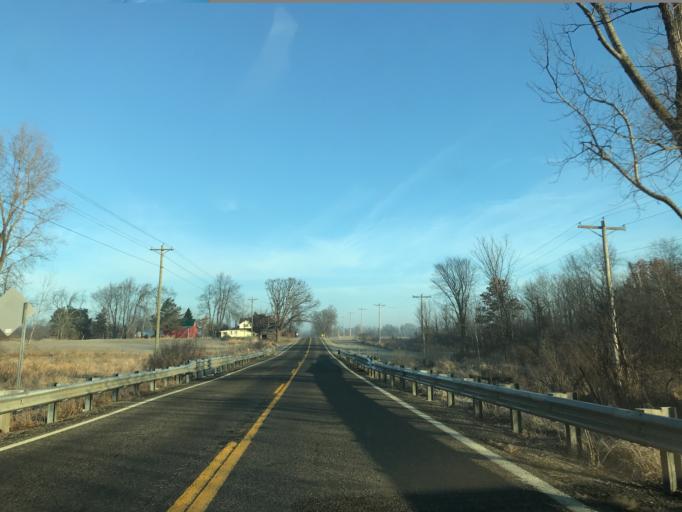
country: US
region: Michigan
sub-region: Eaton County
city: Eaton Rapids
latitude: 42.4806
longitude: -84.6009
